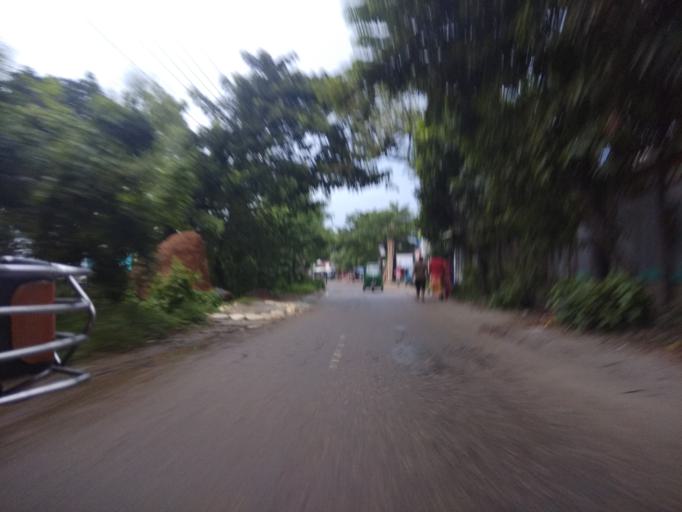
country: BD
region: Dhaka
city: Azimpur
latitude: 23.6711
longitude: 90.2934
